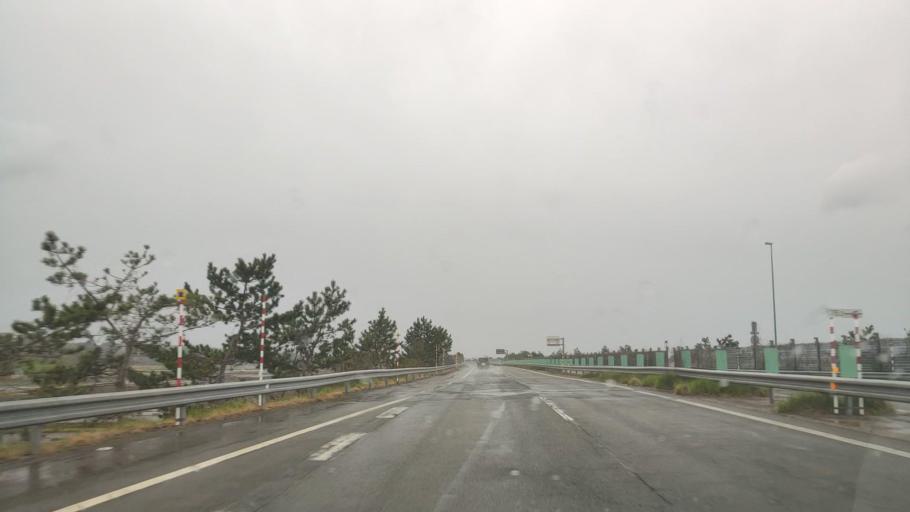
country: JP
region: Akita
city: Noshiromachi
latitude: 40.1840
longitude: 140.0797
